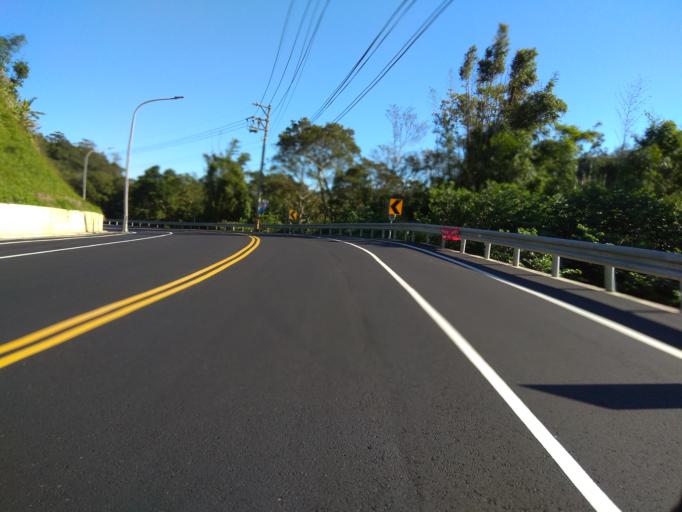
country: TW
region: Taiwan
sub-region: Hsinchu
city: Zhubei
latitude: 24.8488
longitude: 121.1173
